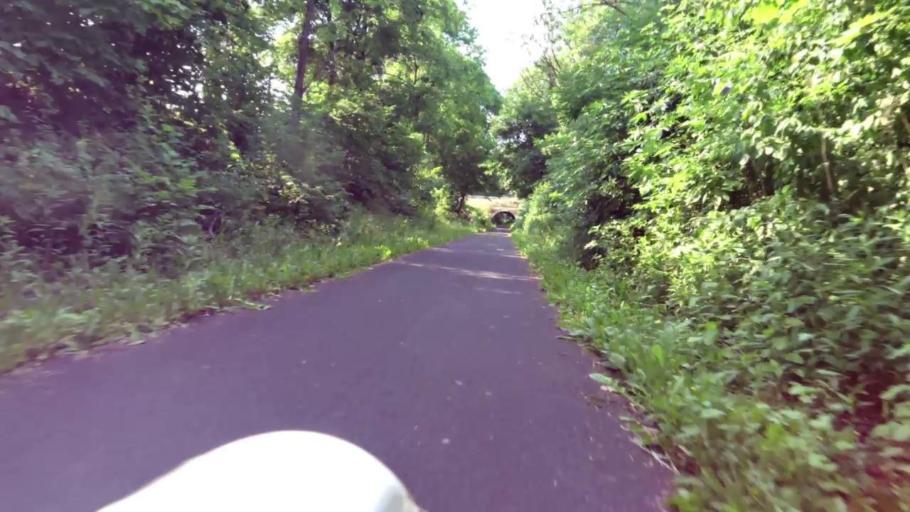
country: PL
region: Kujawsko-Pomorskie
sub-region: Powiat torunski
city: Lubianka
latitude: 53.0846
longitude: 18.5366
